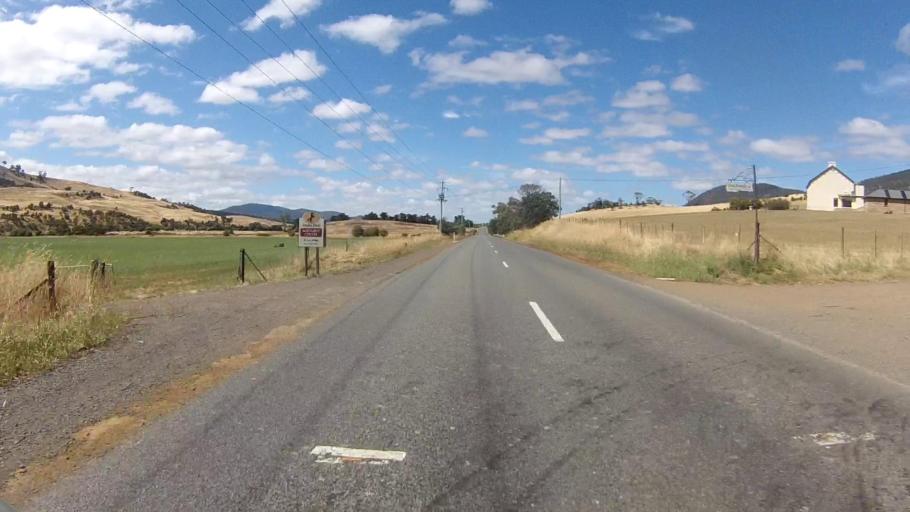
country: AU
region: Tasmania
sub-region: Brighton
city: Bridgewater
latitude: -42.5920
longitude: 147.4112
